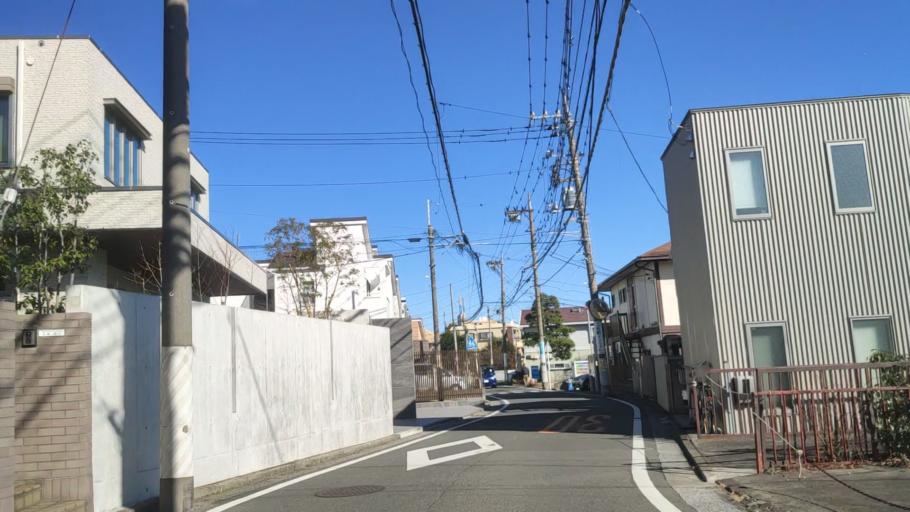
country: JP
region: Kanagawa
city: Yokohama
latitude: 35.4279
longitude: 139.6424
